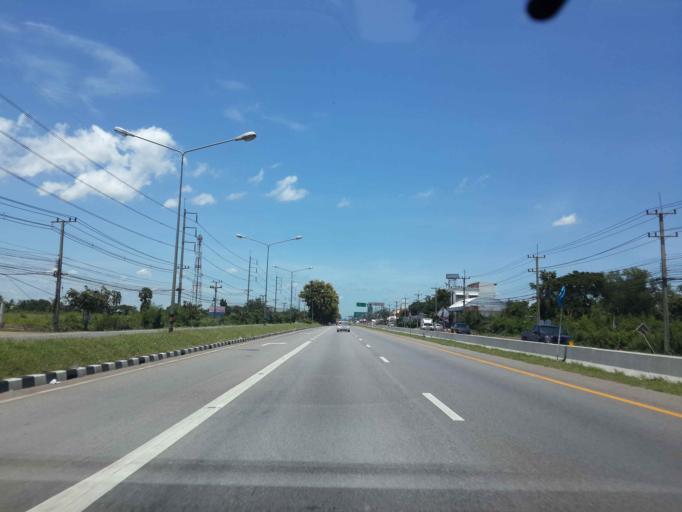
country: TH
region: Phetchaburi
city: Khao Yoi
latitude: 13.2980
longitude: 99.8235
